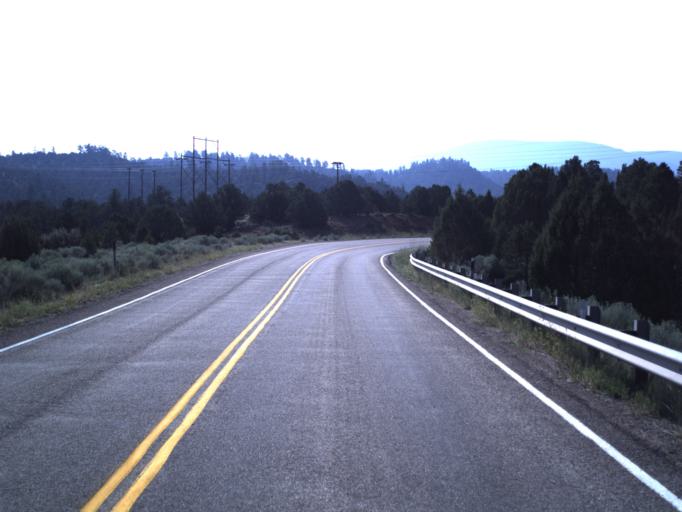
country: US
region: Utah
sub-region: Daggett County
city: Manila
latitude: 40.9070
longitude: -109.4389
